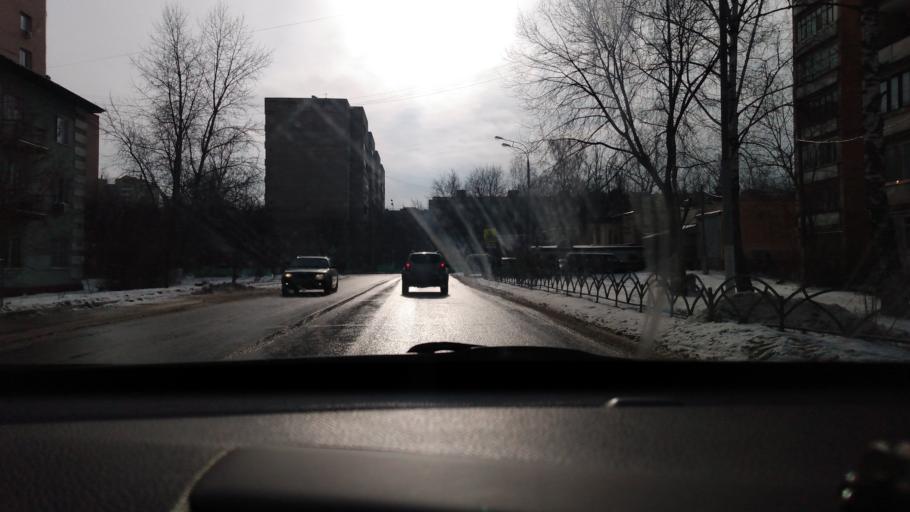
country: RU
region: Moskovskaya
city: Zheleznodorozhnyy
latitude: 55.7496
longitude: 38.0276
